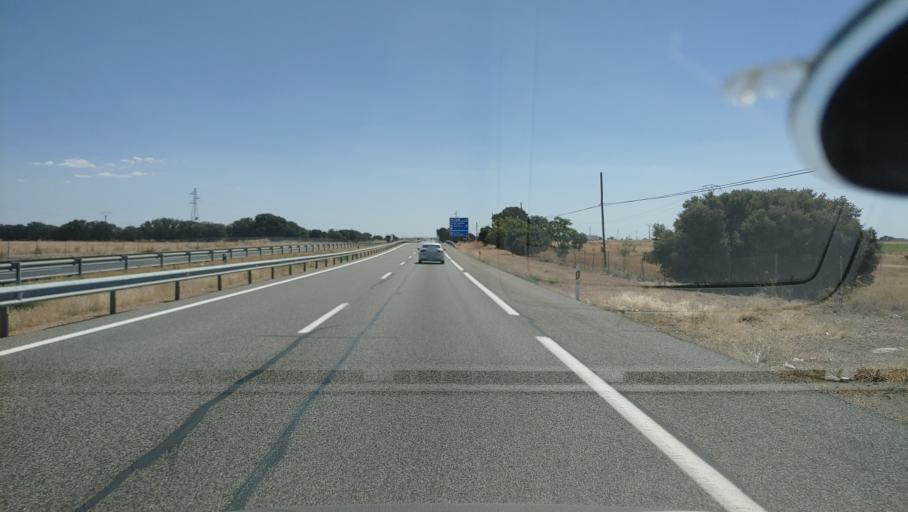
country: ES
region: Castille-La Mancha
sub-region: Provincia de Ciudad Real
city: Villarta de San Juan
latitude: 39.1921
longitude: -3.4026
